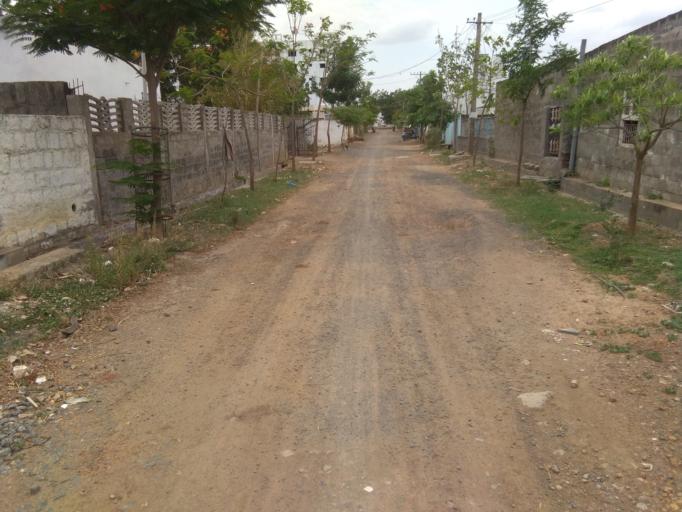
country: IN
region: Andhra Pradesh
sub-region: Guntur
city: Guntur
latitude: 16.3115
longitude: 80.4040
